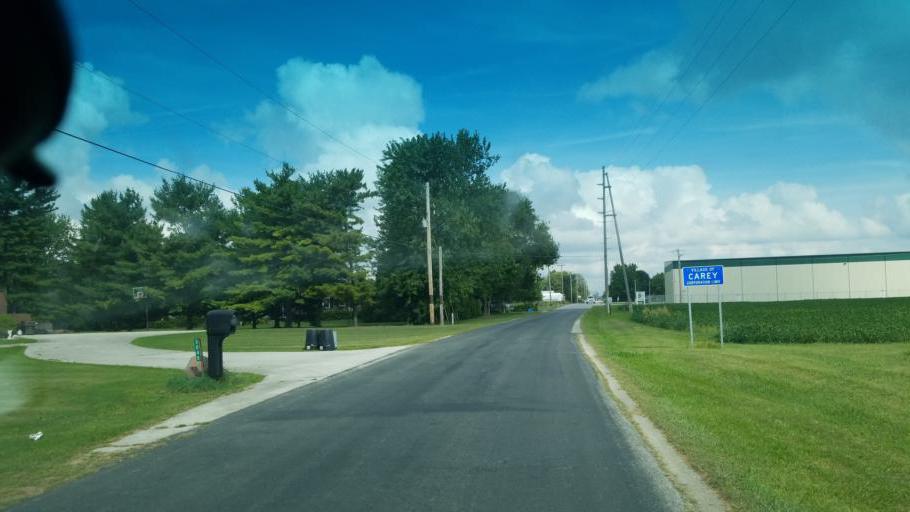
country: US
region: Ohio
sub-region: Wyandot County
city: Carey
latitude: 40.9451
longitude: -83.3675
